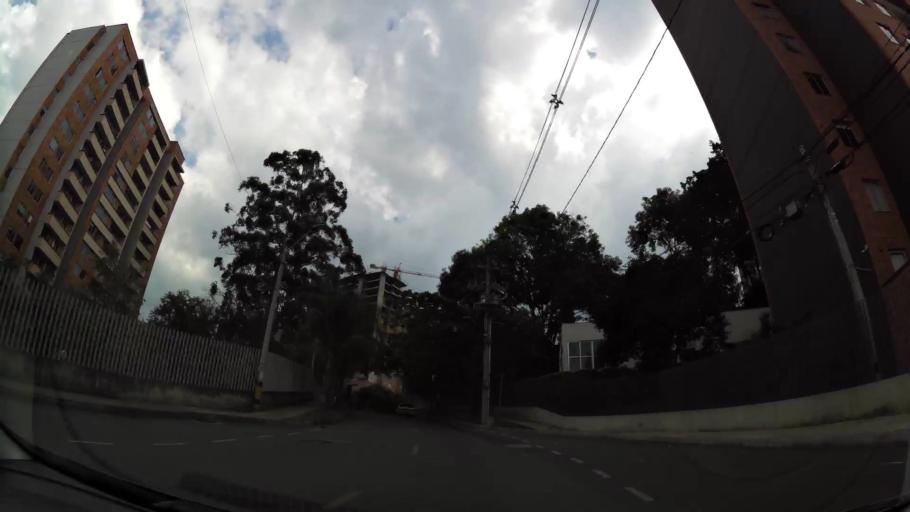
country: CO
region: Antioquia
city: Sabaneta
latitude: 6.1575
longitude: -75.5982
